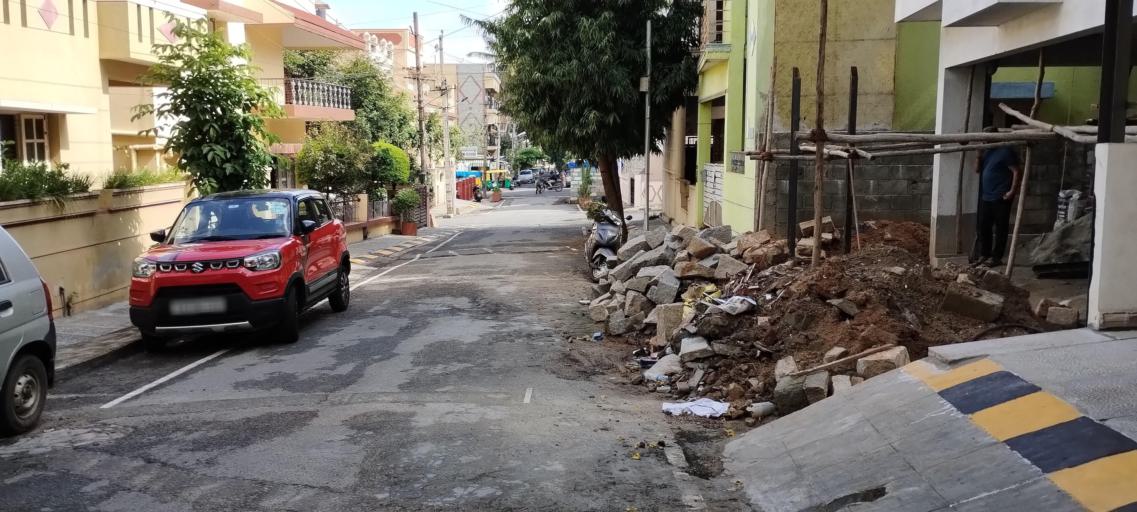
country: IN
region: Karnataka
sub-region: Bangalore Urban
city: Bangalore
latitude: 12.9428
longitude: 77.5391
